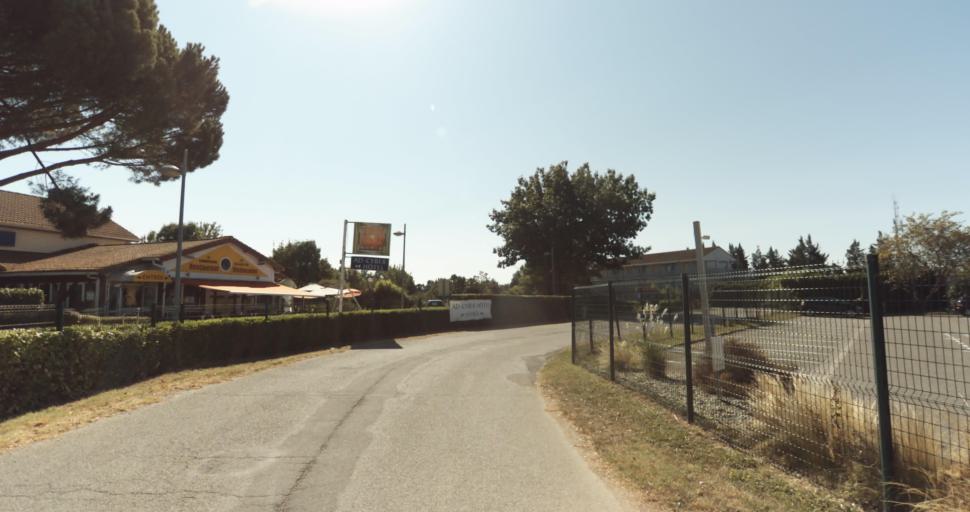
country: FR
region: Midi-Pyrenees
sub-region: Departement de la Haute-Garonne
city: L'Union
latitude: 43.6456
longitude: 1.4718
